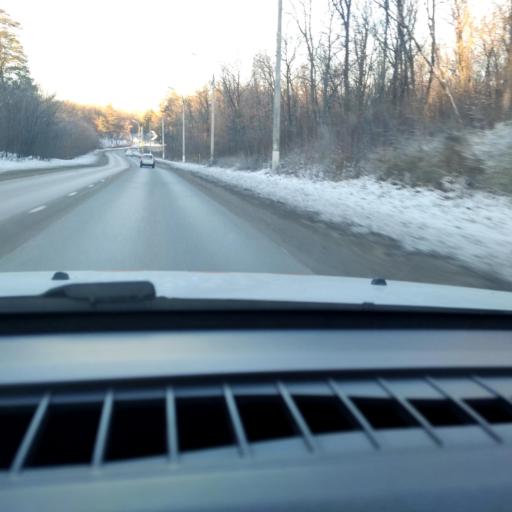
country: RU
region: Samara
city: Tol'yatti
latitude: 53.4933
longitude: 49.2959
